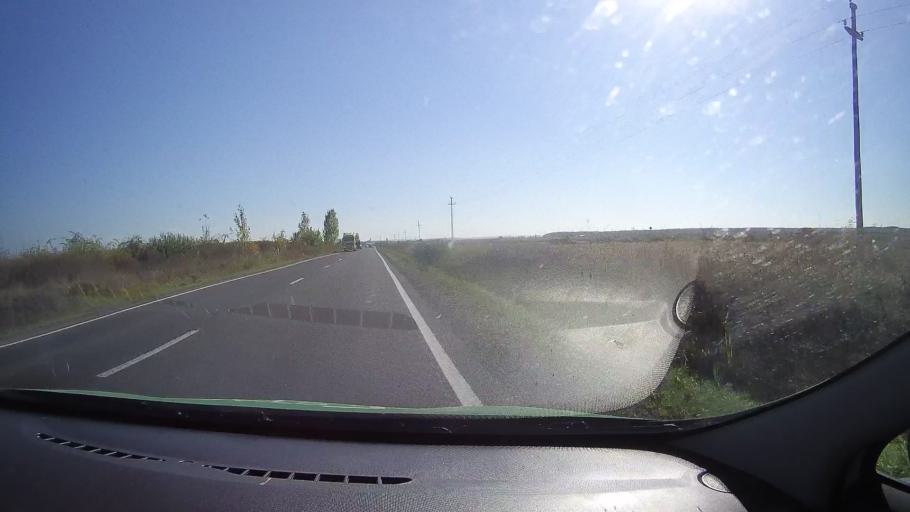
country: RO
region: Satu Mare
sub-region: Oras Ardud
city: Madaras
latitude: 47.6612
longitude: 22.8732
